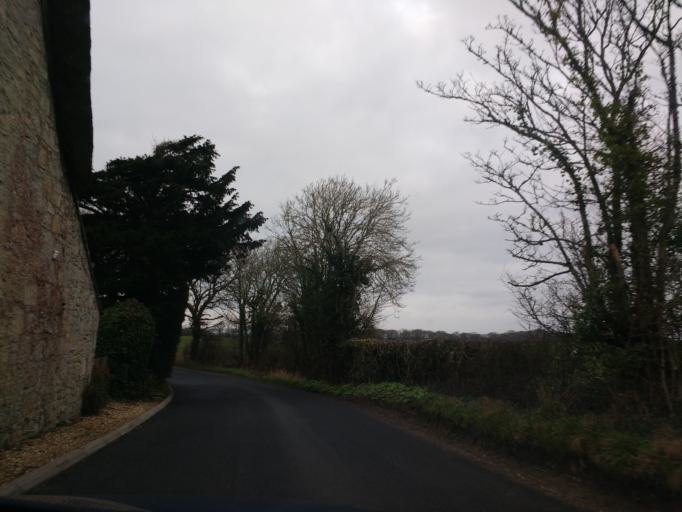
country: GB
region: England
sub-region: Isle of Wight
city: Shalfleet
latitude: 50.6896
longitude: -1.3997
